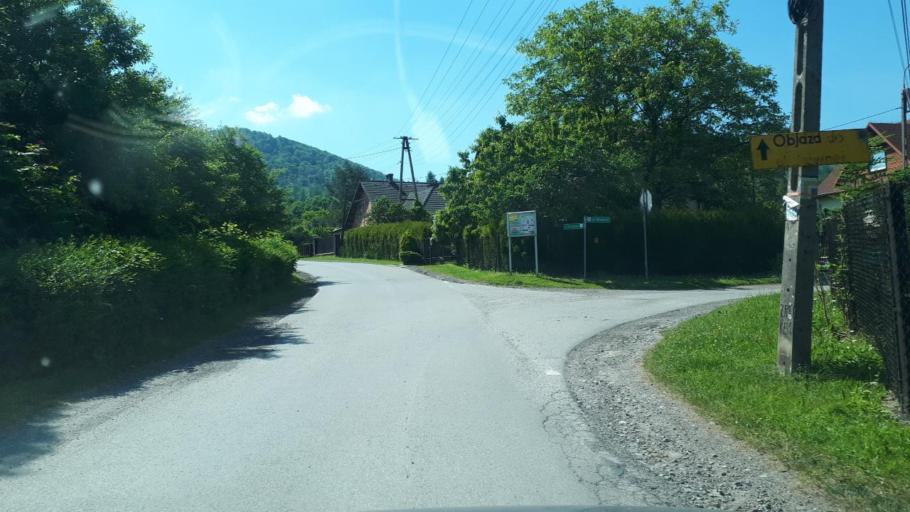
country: PL
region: Silesian Voivodeship
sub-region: Powiat bielski
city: Jaworze
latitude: 49.7870
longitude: 18.9451
